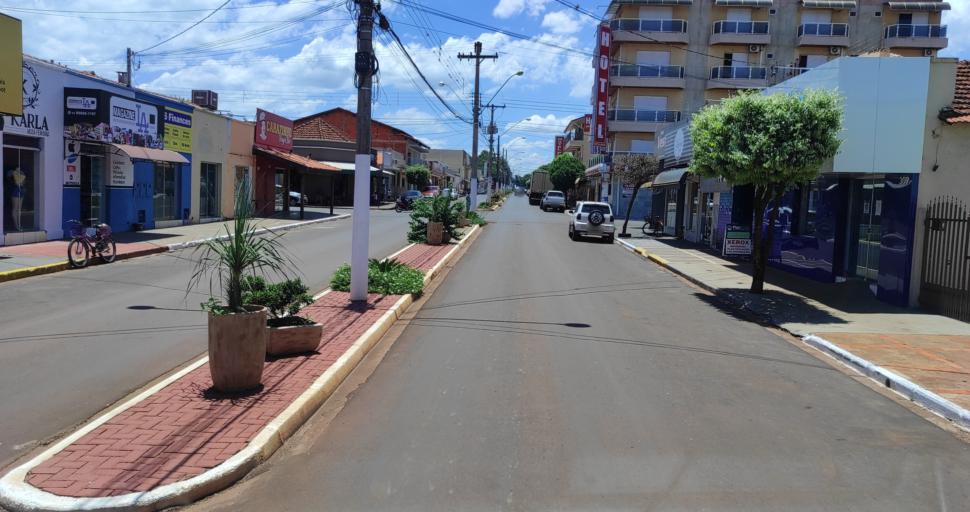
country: BR
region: Minas Gerais
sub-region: Frutal
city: Frutal
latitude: -20.1396
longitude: -48.7009
